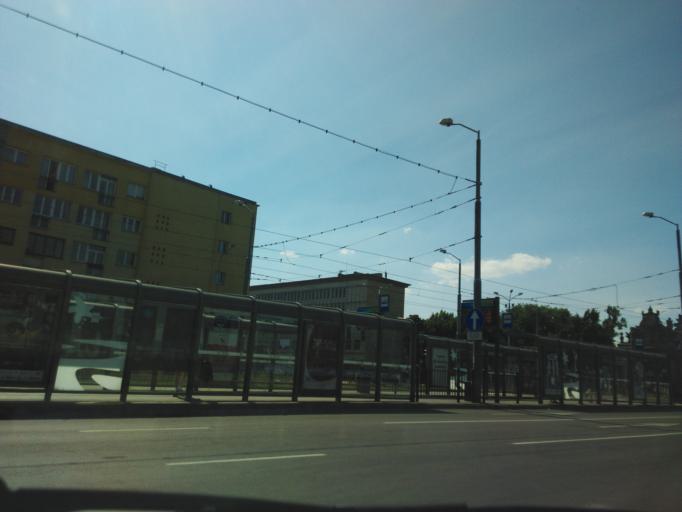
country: PL
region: West Pomeranian Voivodeship
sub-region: Szczecin
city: Szczecin
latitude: 53.4249
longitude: 14.5521
